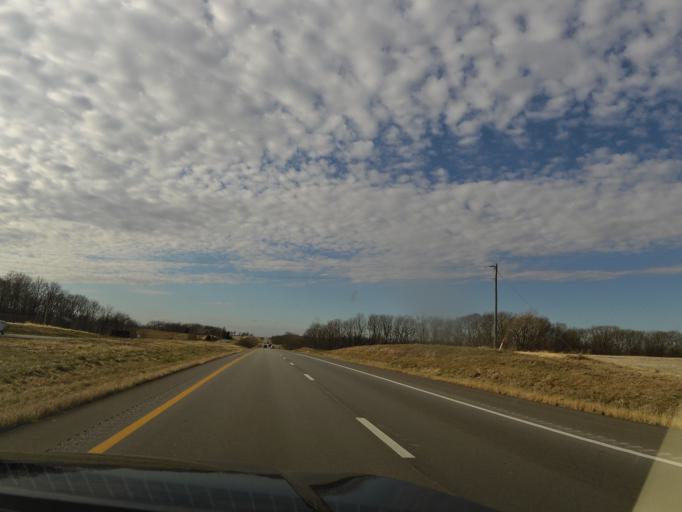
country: US
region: Missouri
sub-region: Marion County
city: Palmyra
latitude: 39.7439
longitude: -91.4449
